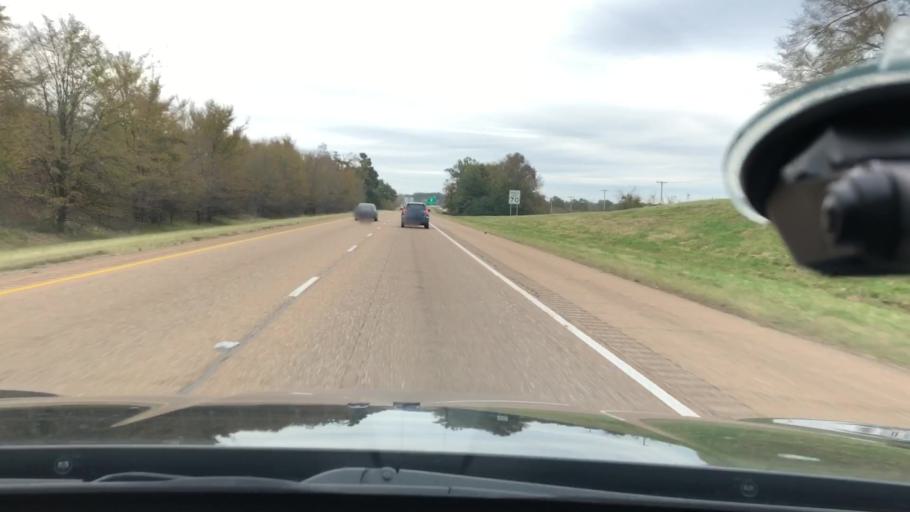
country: US
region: Arkansas
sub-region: Nevada County
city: Prescott
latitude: 33.8175
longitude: -93.4137
